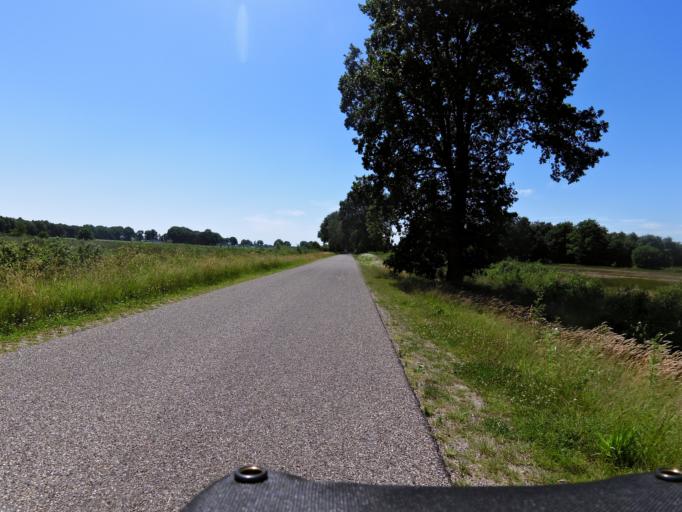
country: NL
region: Overijssel
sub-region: Gemeente Twenterand
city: Magele
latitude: 52.5003
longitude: 6.5383
